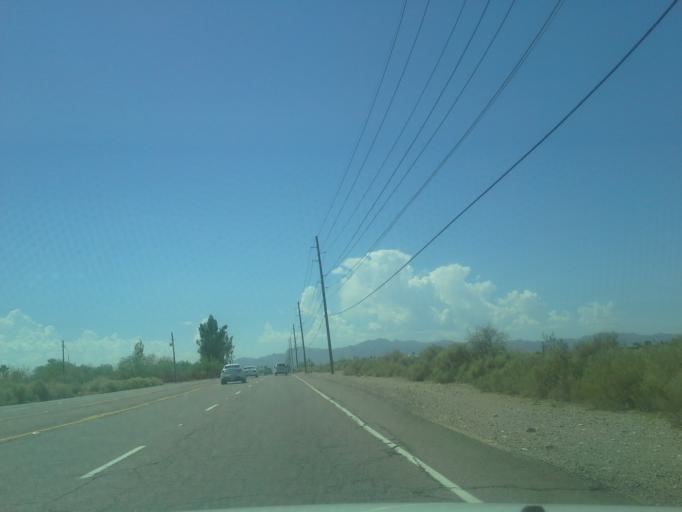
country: US
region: Arizona
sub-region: Maricopa County
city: Litchfield Park
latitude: 33.5367
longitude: -112.3308
